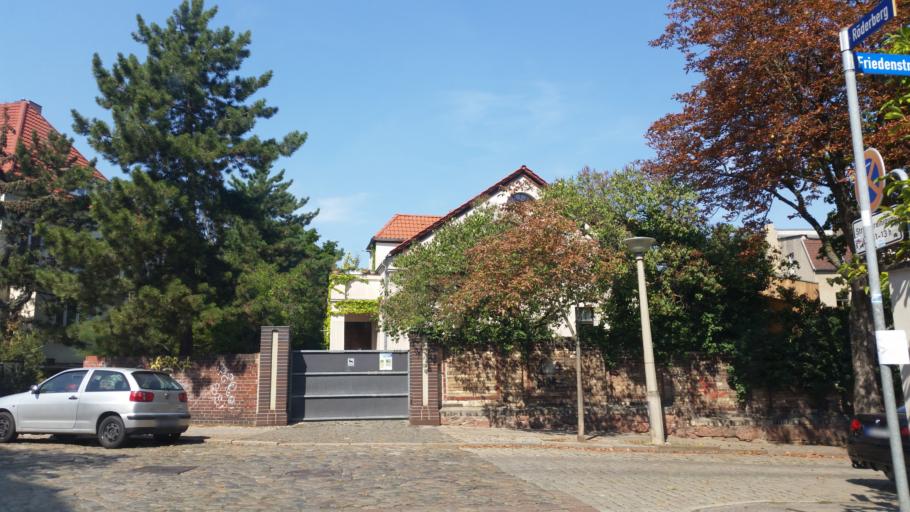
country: DE
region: Saxony-Anhalt
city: Halle (Saale)
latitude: 51.5030
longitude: 11.9659
